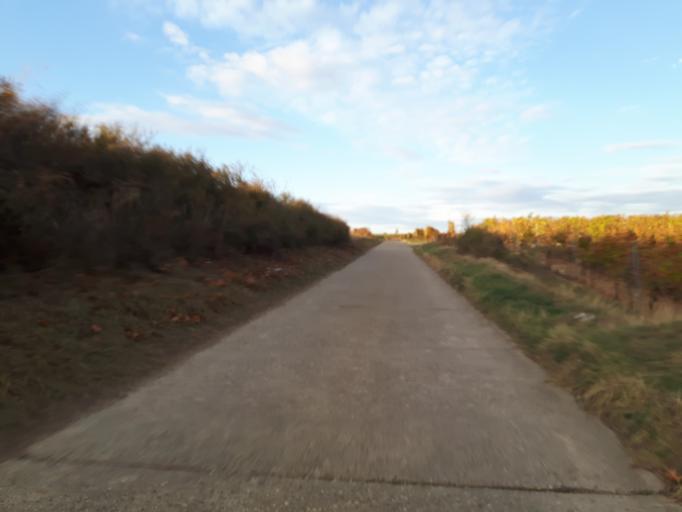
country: DE
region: Rheinland-Pfalz
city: Bockenheim
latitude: 49.6224
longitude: 8.1804
